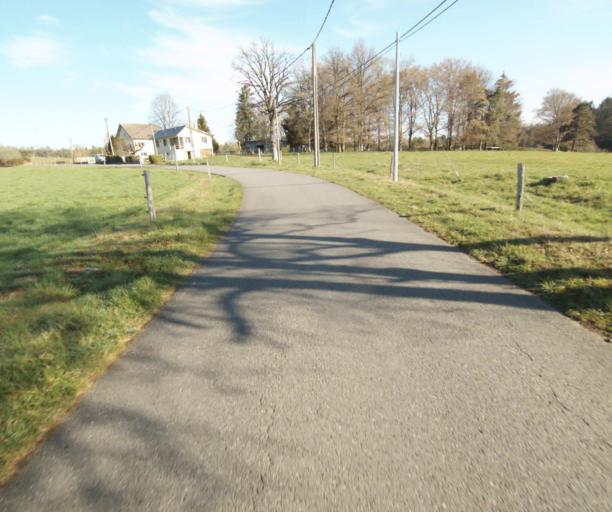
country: FR
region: Limousin
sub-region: Departement de la Correze
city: Correze
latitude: 45.3197
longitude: 1.8883
